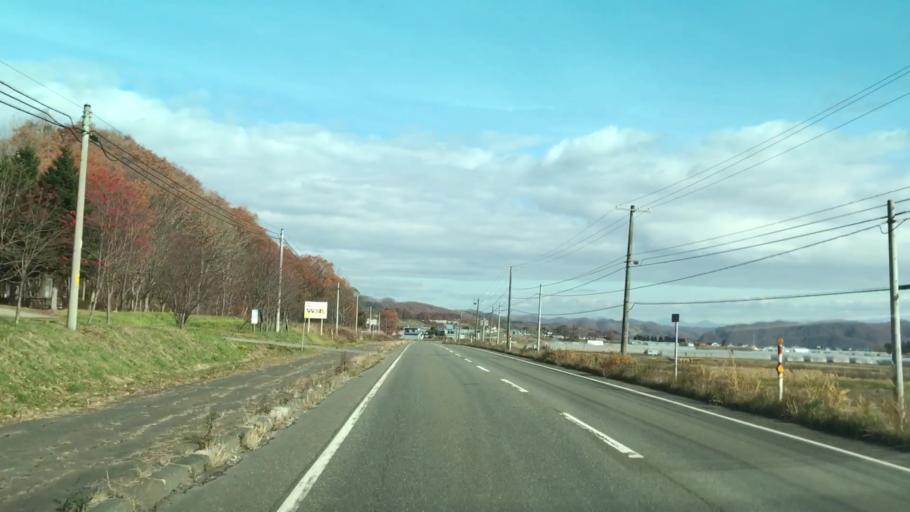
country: JP
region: Hokkaido
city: Shizunai-furukawacho
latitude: 42.5677
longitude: 142.0948
